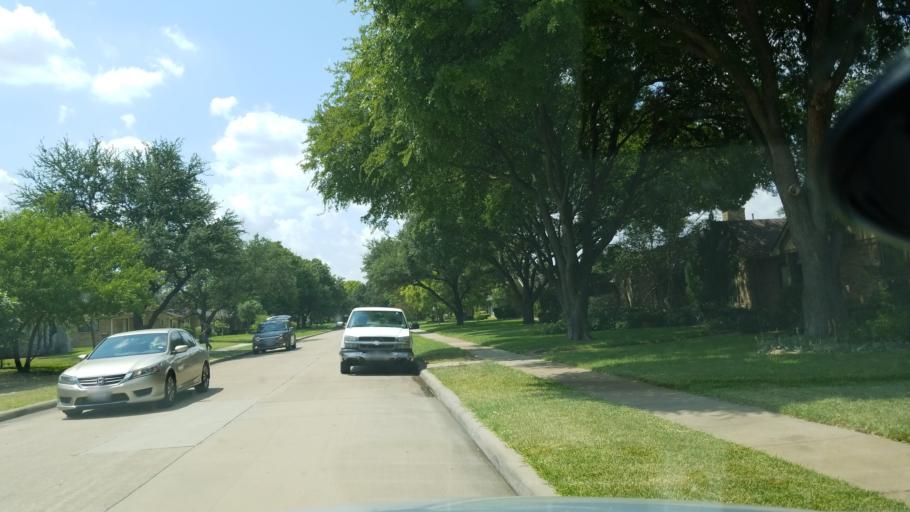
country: US
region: Texas
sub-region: Dallas County
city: Richardson
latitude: 32.9276
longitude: -96.7207
